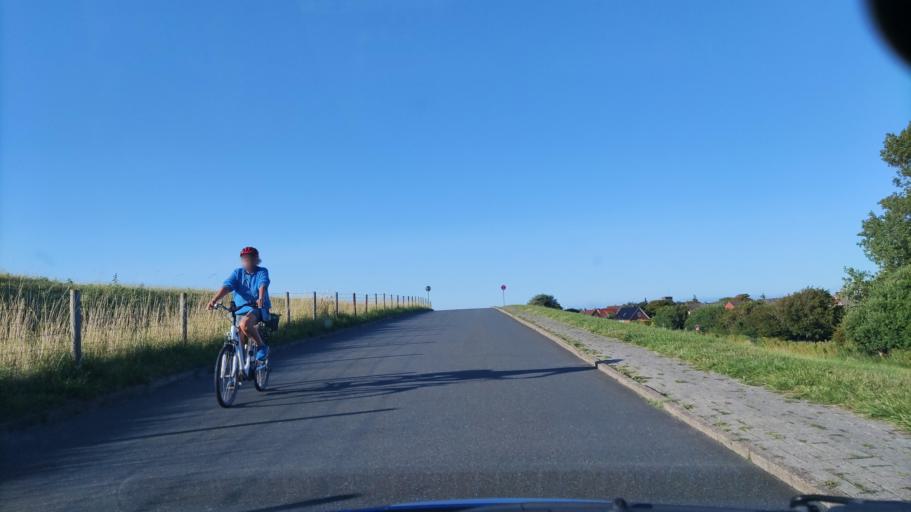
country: DE
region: Lower Saxony
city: Werdum
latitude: 53.7044
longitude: 7.8031
